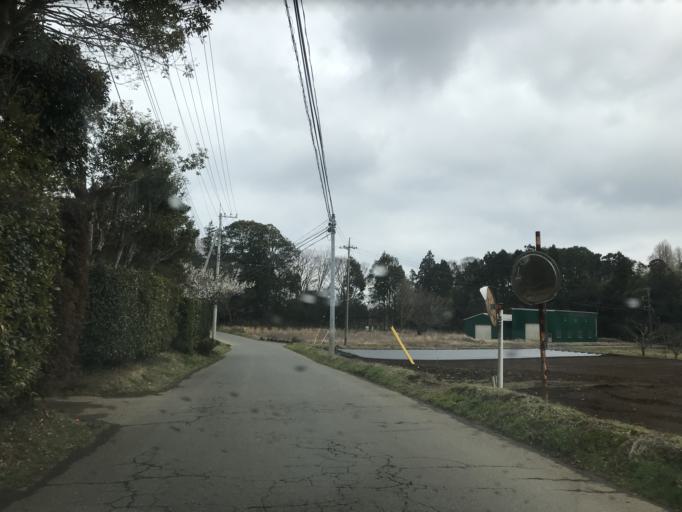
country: JP
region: Chiba
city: Sawara
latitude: 35.8476
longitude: 140.5127
